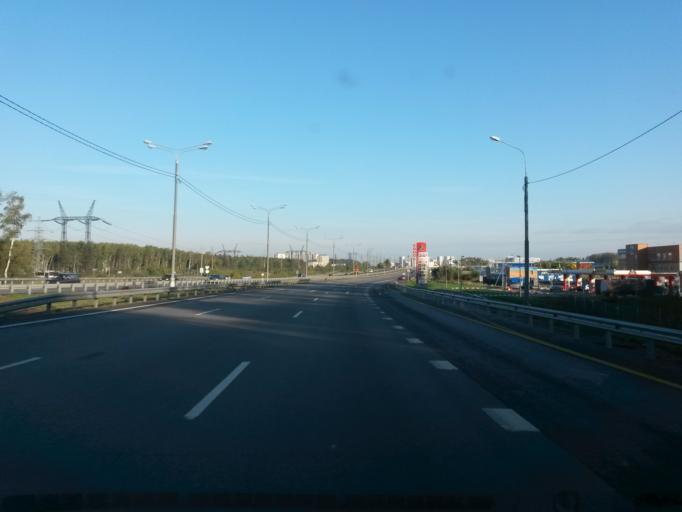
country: RU
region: Moskovskaya
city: Vostryakovo
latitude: 55.3670
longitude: 37.7839
